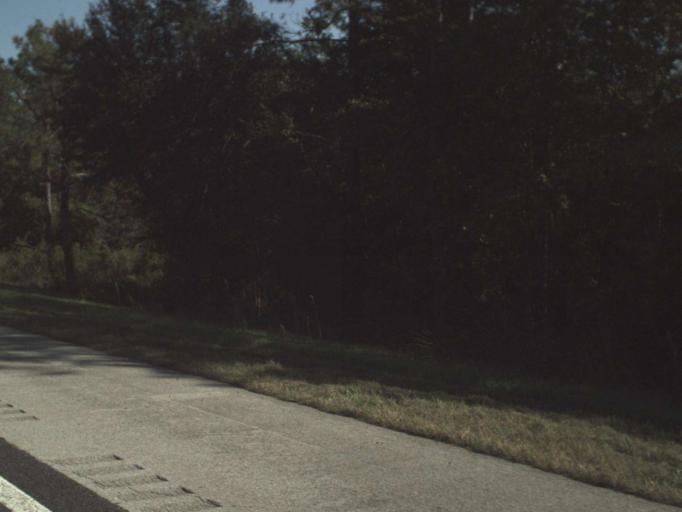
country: US
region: Florida
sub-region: Holmes County
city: Bonifay
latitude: 30.7599
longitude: -85.7430
